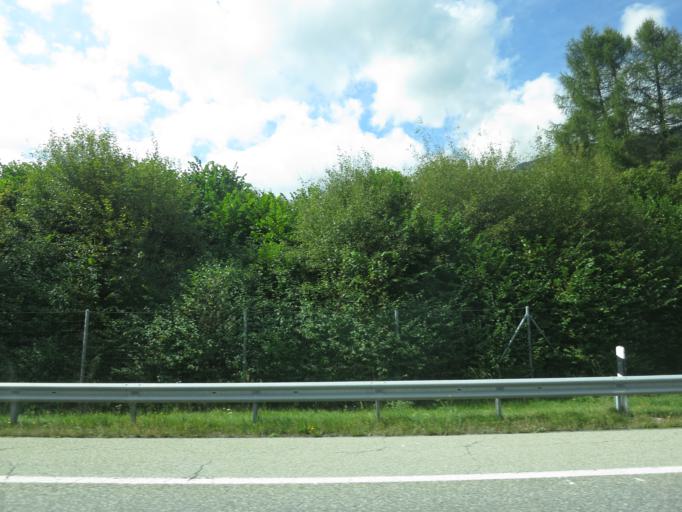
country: CH
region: Grisons
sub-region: Hinterrhein District
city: Thusis
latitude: 46.6331
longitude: 9.4383
